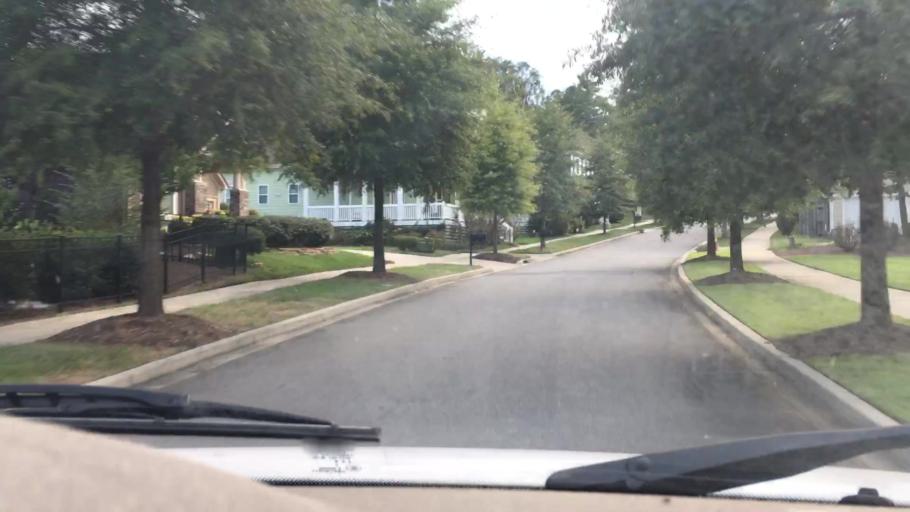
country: US
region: North Carolina
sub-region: Mecklenburg County
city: Huntersville
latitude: 35.4115
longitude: -80.8318
